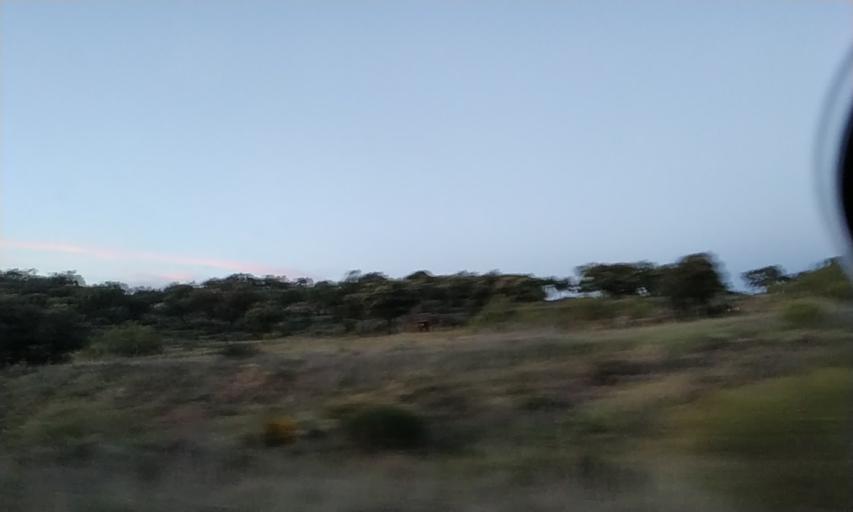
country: ES
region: Extremadura
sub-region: Provincia de Caceres
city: Piedras Albas
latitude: 39.7713
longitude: -6.9158
